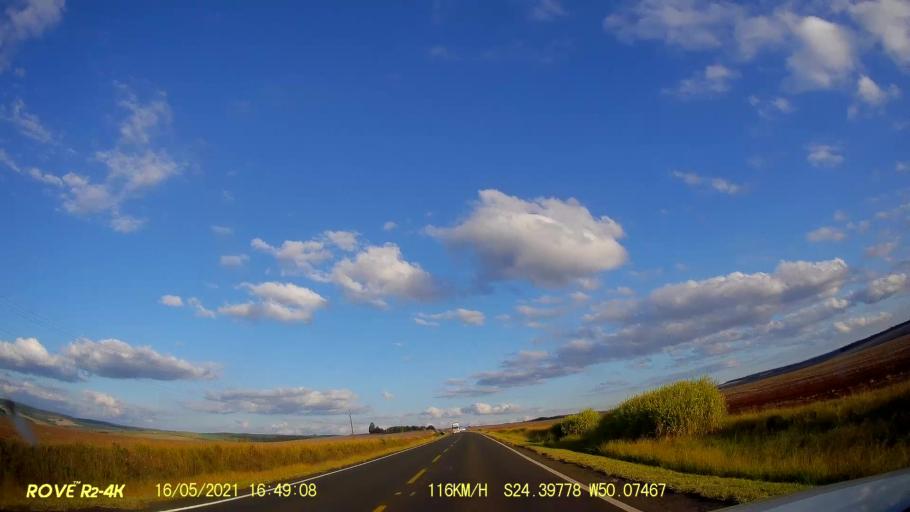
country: BR
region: Parana
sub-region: Pirai Do Sul
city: Pirai do Sul
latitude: -24.3978
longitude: -50.0746
